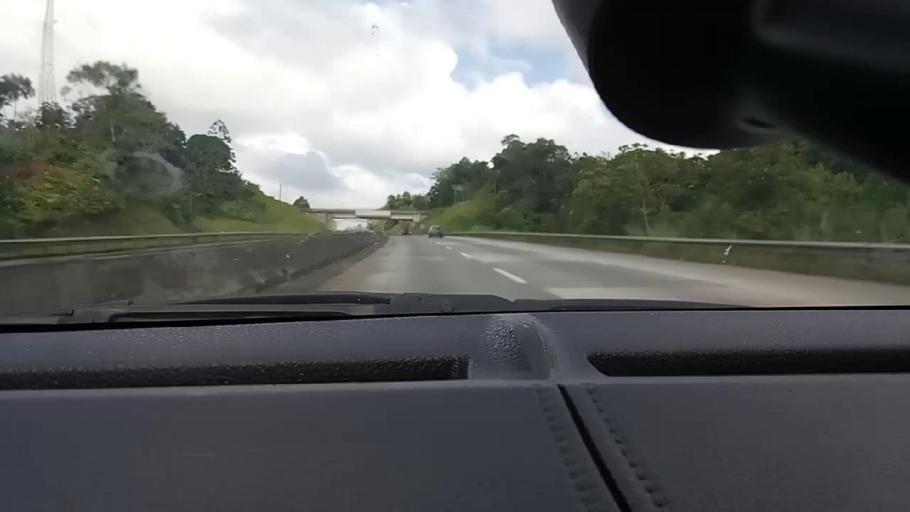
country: PA
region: Colon
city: Gatun
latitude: 9.2921
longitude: -79.7820
